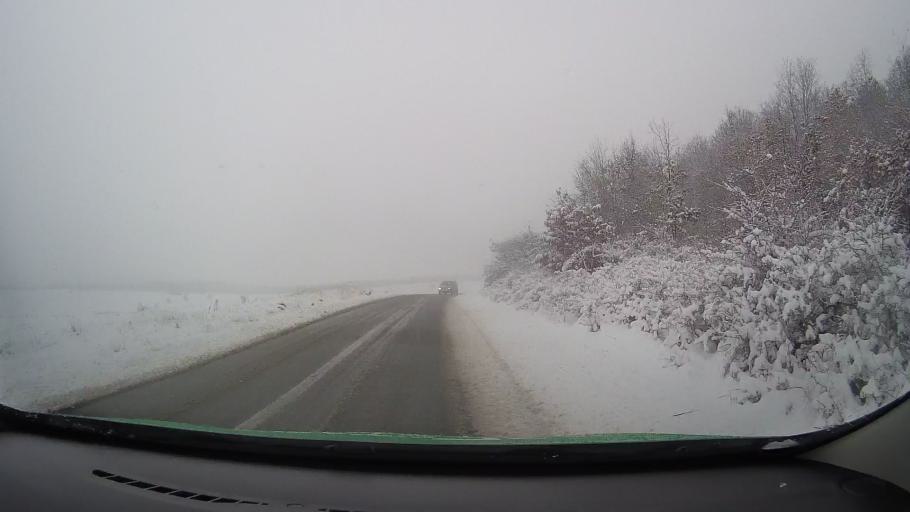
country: RO
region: Hunedoara
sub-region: Comuna Teliucu Inferior
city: Teliucu Inferior
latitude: 45.6876
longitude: 22.9087
